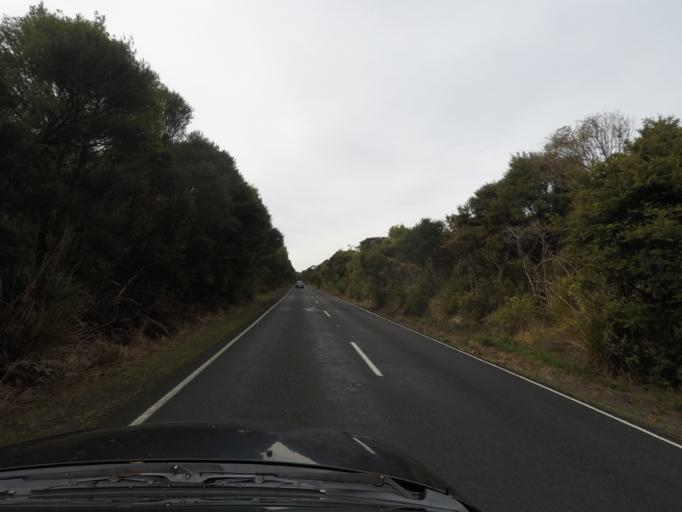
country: NZ
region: Auckland
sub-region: Auckland
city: Titirangi
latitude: -36.9353
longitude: 174.5621
